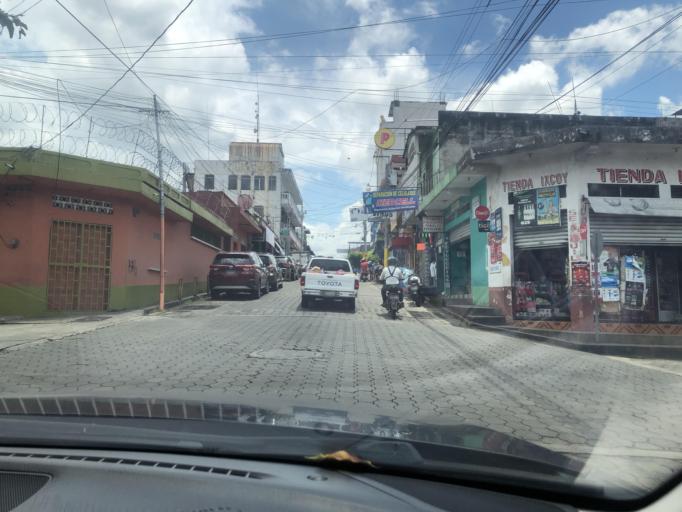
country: GT
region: Quetzaltenango
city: Coatepeque
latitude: 14.7033
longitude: -91.8659
